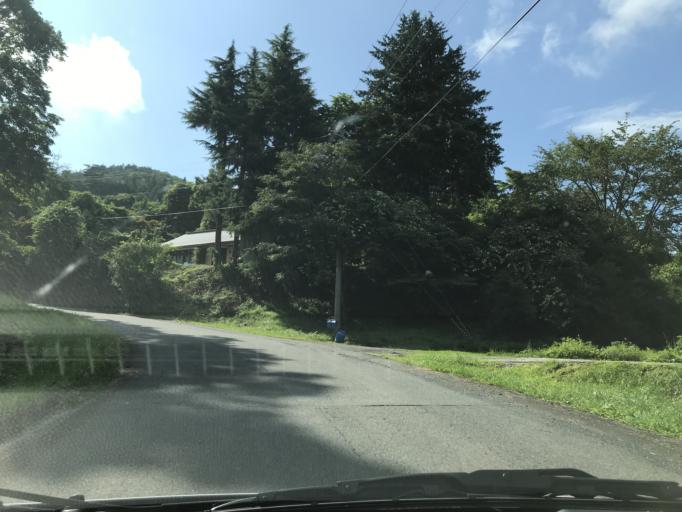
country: JP
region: Iwate
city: Mizusawa
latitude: 39.0260
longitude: 141.1915
